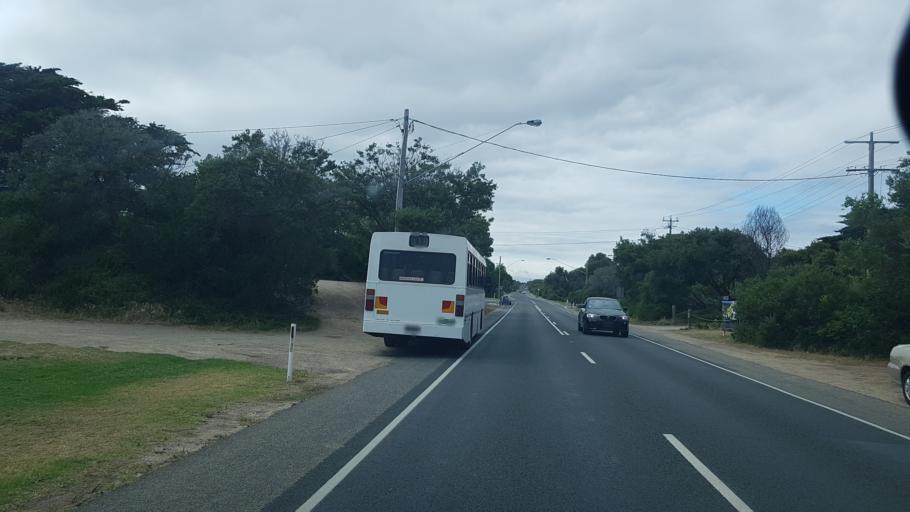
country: AU
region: Victoria
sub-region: Mornington Peninsula
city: Sorrento
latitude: -38.3471
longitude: 144.7412
